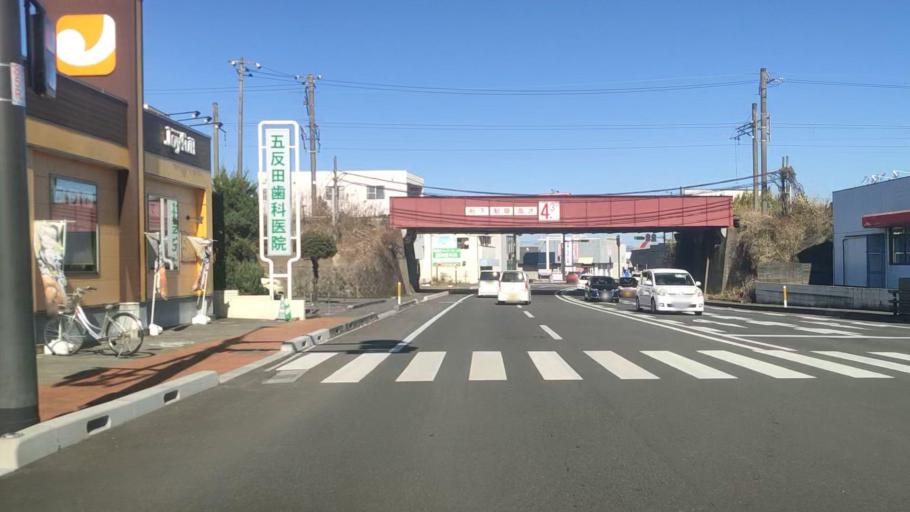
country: JP
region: Miyazaki
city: Miyakonojo
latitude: 31.7366
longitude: 131.0691
